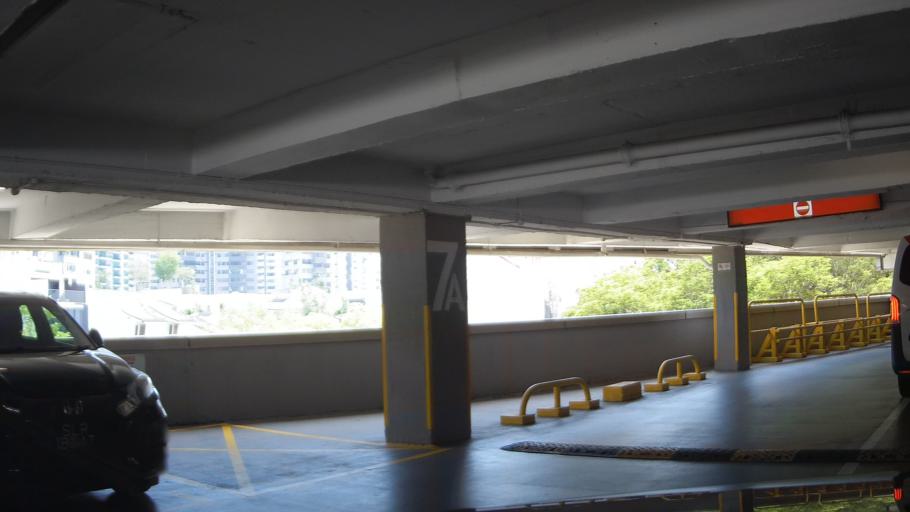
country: SG
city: Singapore
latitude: 1.2711
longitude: 103.8418
